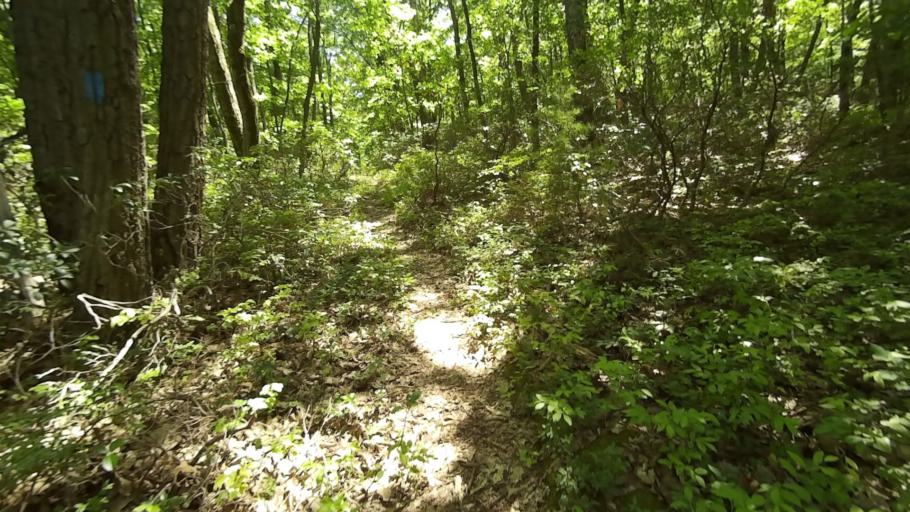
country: US
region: Pennsylvania
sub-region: Centre County
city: Boalsburg
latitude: 40.7209
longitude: -77.7695
